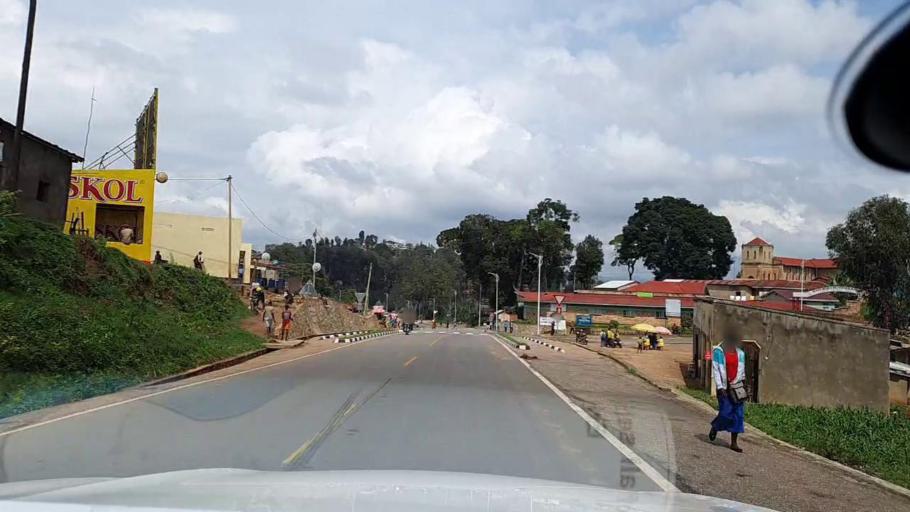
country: RW
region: Southern Province
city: Nzega
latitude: -2.4850
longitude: 29.5291
